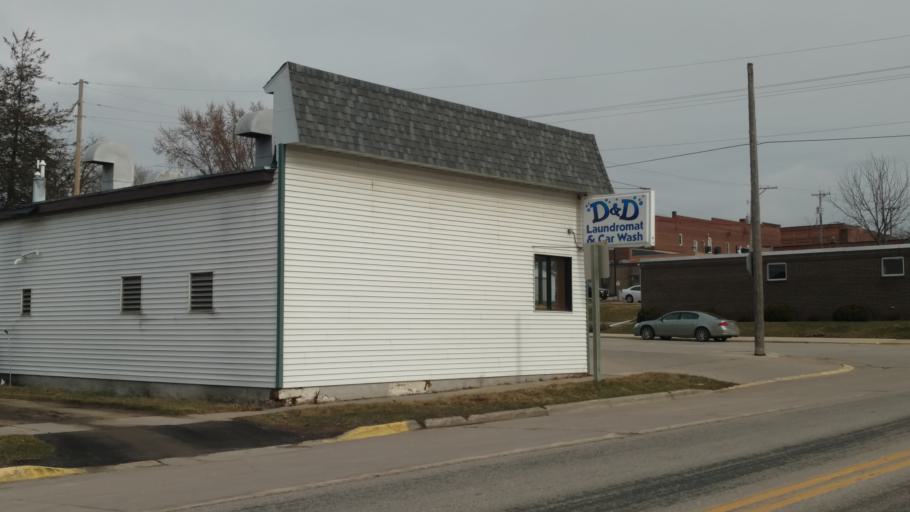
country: US
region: Wisconsin
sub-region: Vernon County
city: Hillsboro
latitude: 43.6497
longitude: -90.3411
